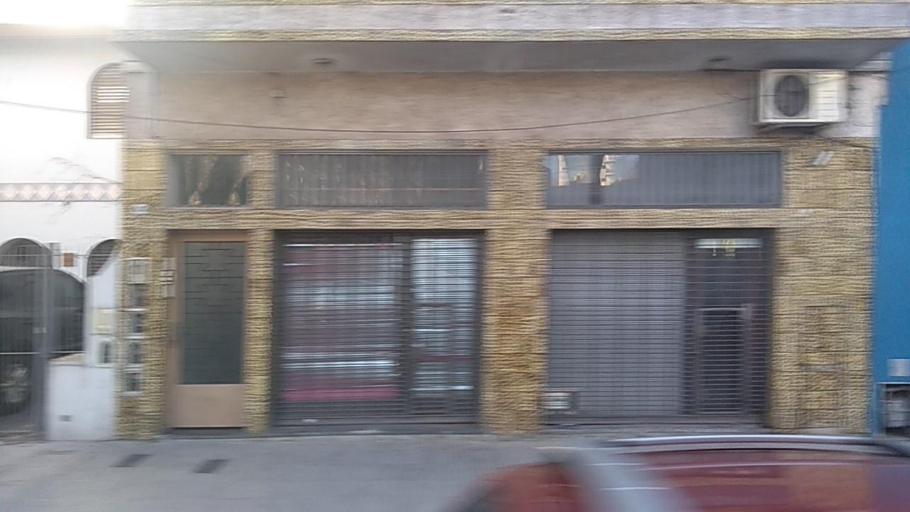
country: AR
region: Buenos Aires F.D.
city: Villa Santa Rita
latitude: -34.6225
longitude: -58.5084
